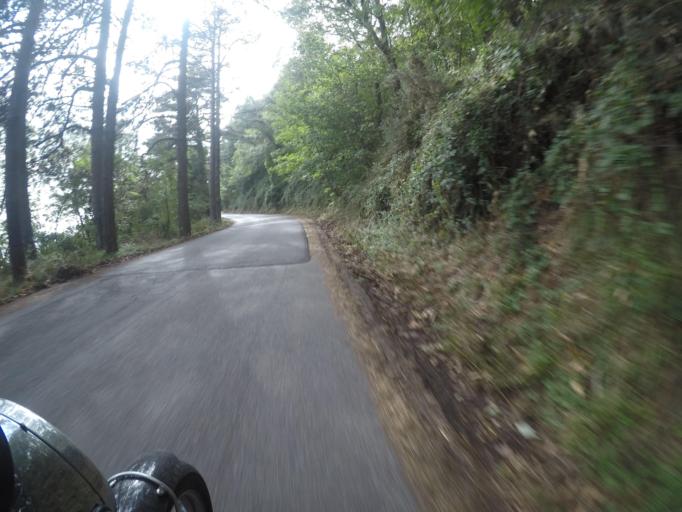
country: IT
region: Tuscany
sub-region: Provincia di Massa-Carrara
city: Fosdinovo
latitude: 44.1206
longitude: 10.0718
